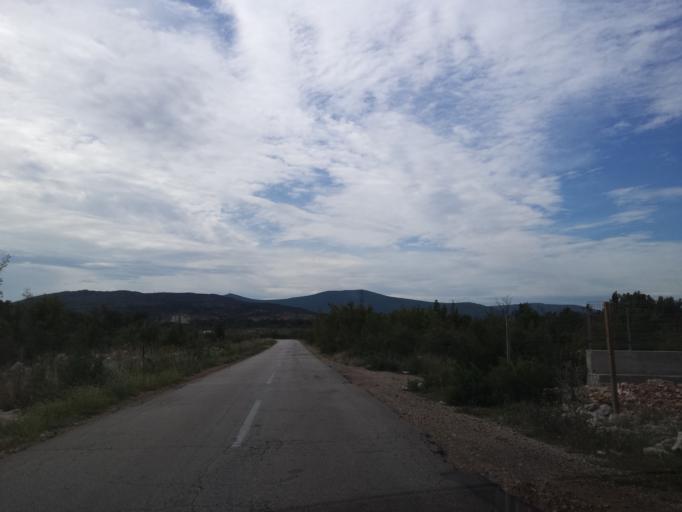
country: BA
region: Federation of Bosnia and Herzegovina
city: Capljina
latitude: 43.1777
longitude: 17.6490
